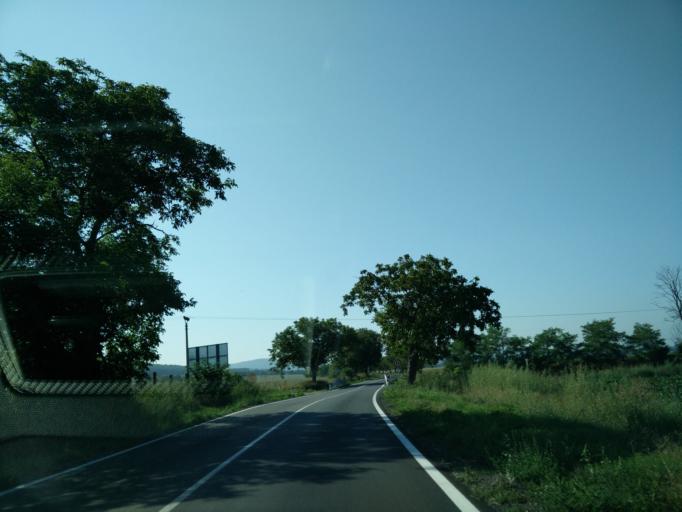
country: SK
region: Nitriansky
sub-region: Okres Nitra
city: Nitra
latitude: 48.4598
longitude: 18.1433
